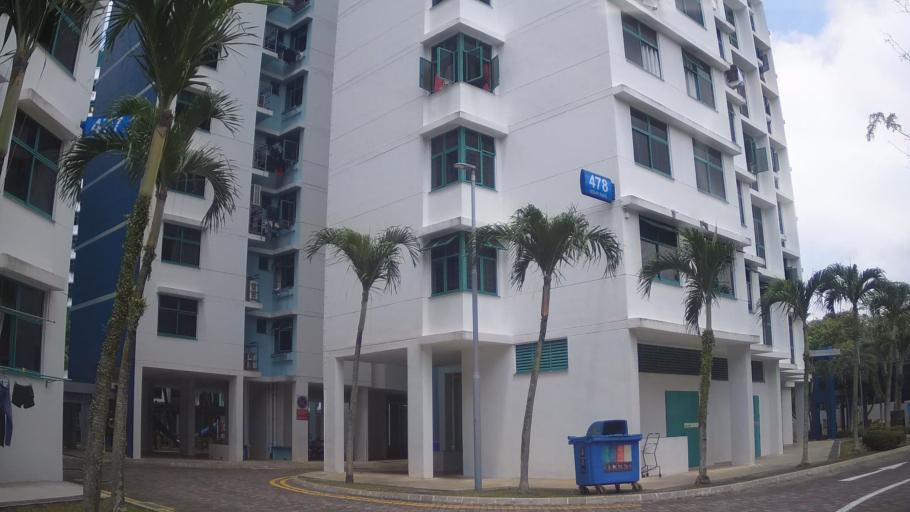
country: MY
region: Johor
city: Johor Bahru
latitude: 1.3895
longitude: 103.7733
